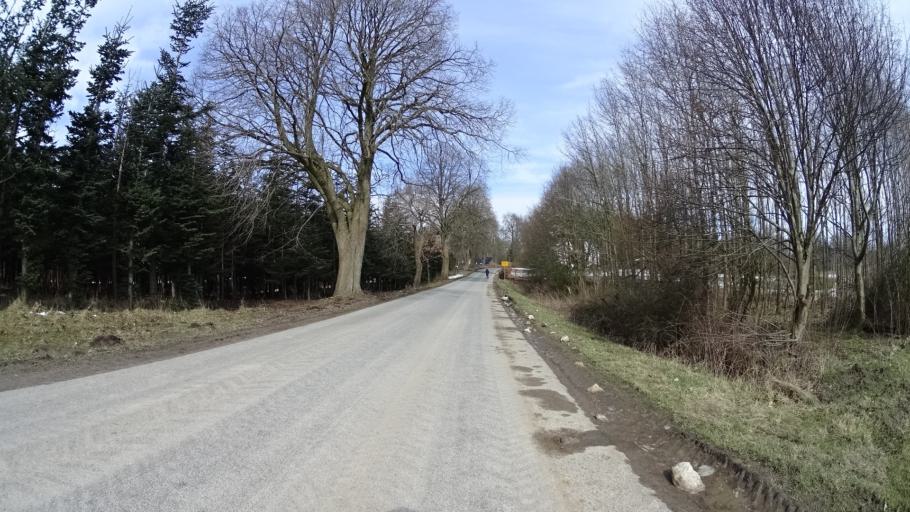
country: DE
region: Schleswig-Holstein
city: Stolpe
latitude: 54.1548
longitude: 10.2344
